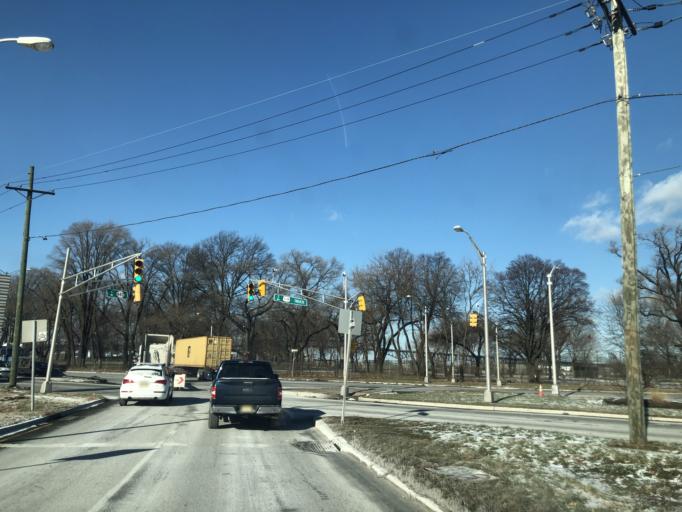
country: US
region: New Jersey
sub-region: Hudson County
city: Jersey City
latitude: 40.7239
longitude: -74.0908
